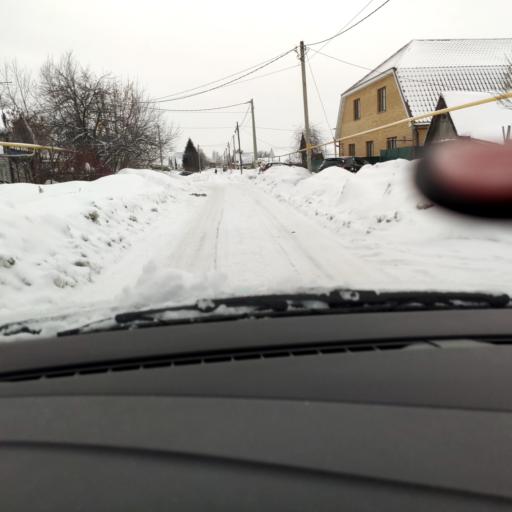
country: RU
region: Tatarstan
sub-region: Gorod Kazan'
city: Kazan
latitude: 55.7266
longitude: 49.0851
